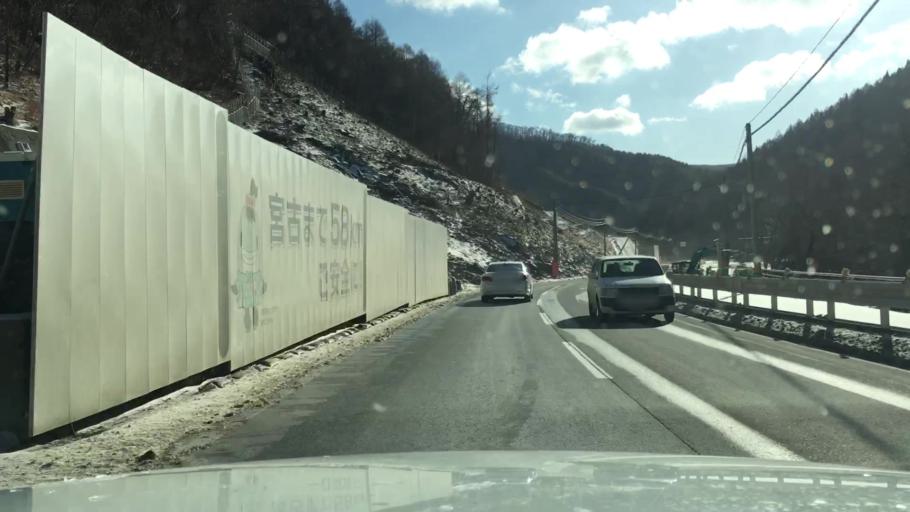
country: JP
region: Iwate
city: Tono
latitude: 39.6261
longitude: 141.4686
